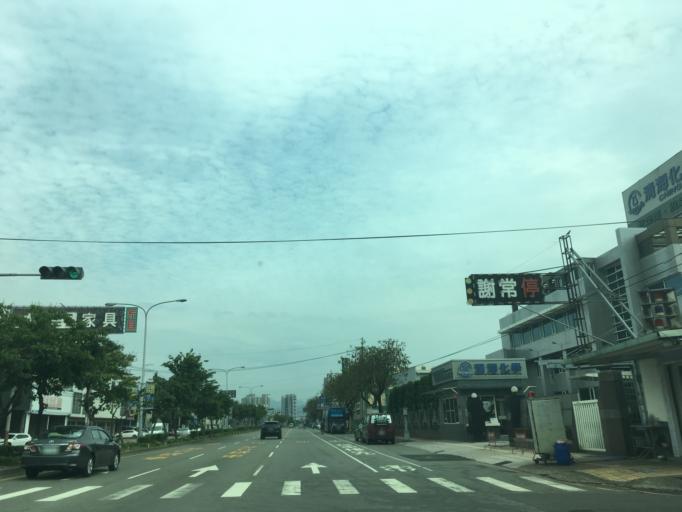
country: TW
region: Taiwan
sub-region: Taichung City
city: Taichung
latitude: 24.1068
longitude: 120.6642
